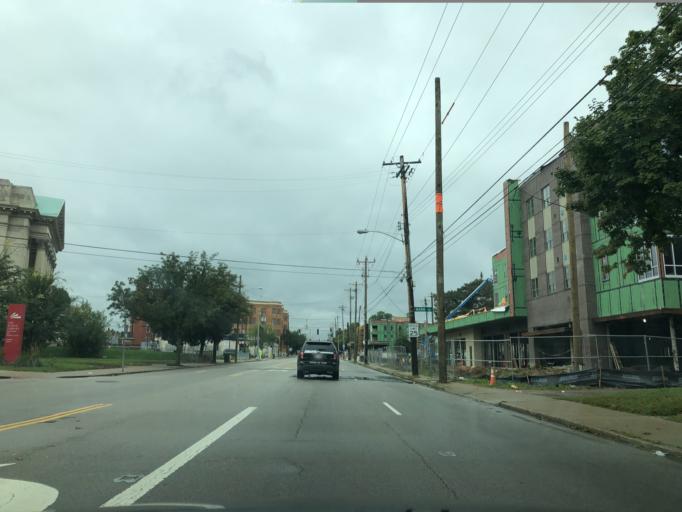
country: US
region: Ohio
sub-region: Hamilton County
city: Saint Bernard
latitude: 39.1473
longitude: -84.4892
